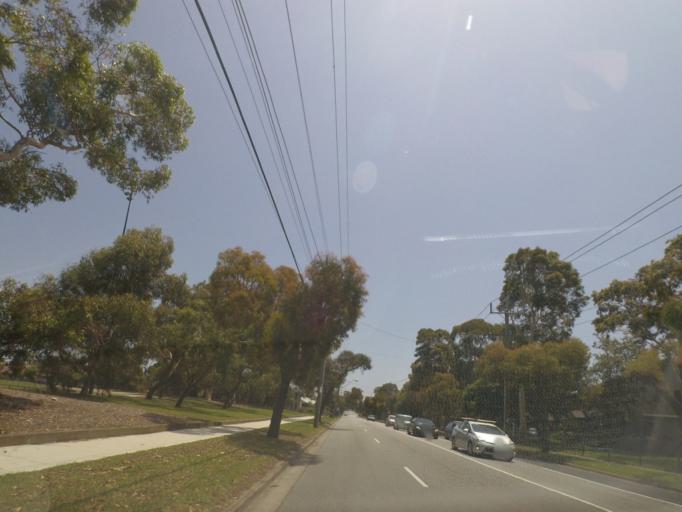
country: AU
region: Victoria
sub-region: Bayside
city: Hampton East
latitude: -37.9428
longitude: 145.0228
